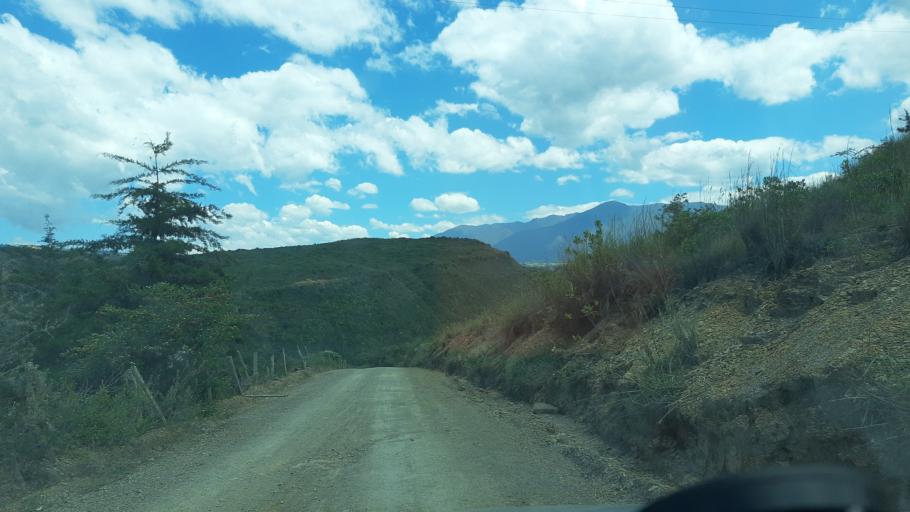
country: CO
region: Boyaca
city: Villa de Leiva
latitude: 5.6764
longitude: -73.5680
